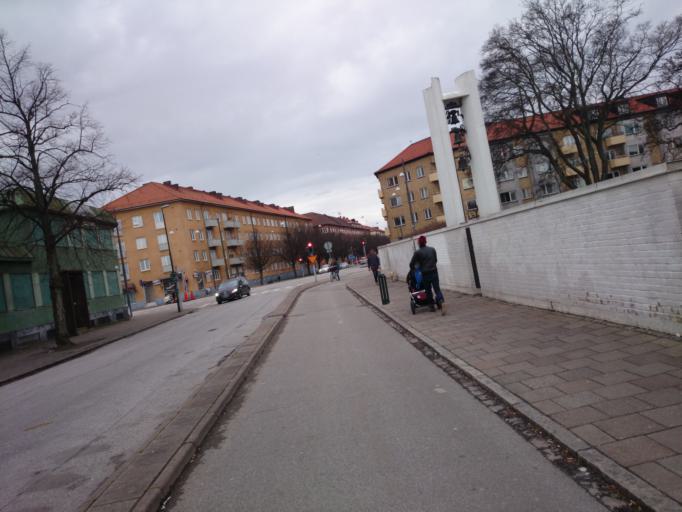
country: SE
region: Skane
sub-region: Malmo
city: Malmoe
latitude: 55.5888
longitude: 13.0208
